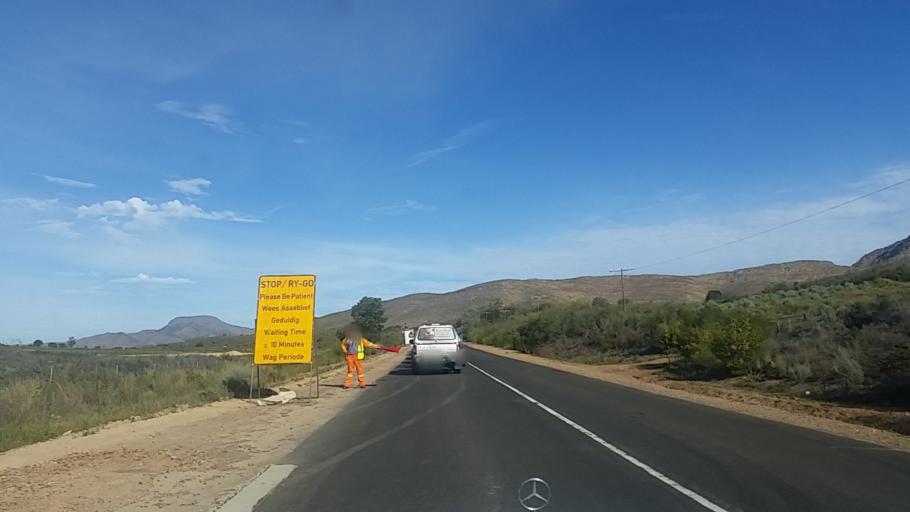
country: ZA
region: Western Cape
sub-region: Eden District Municipality
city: George
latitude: -33.8231
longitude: 22.3841
